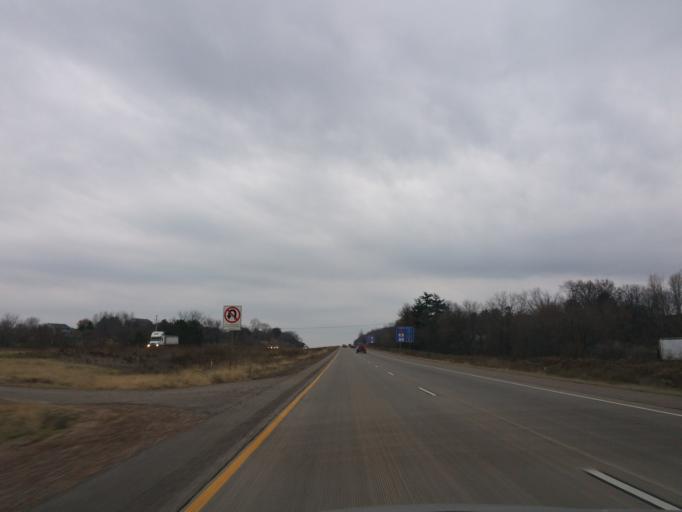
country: US
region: Wisconsin
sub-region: Eau Claire County
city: Eau Claire
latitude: 44.8091
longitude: -91.5604
